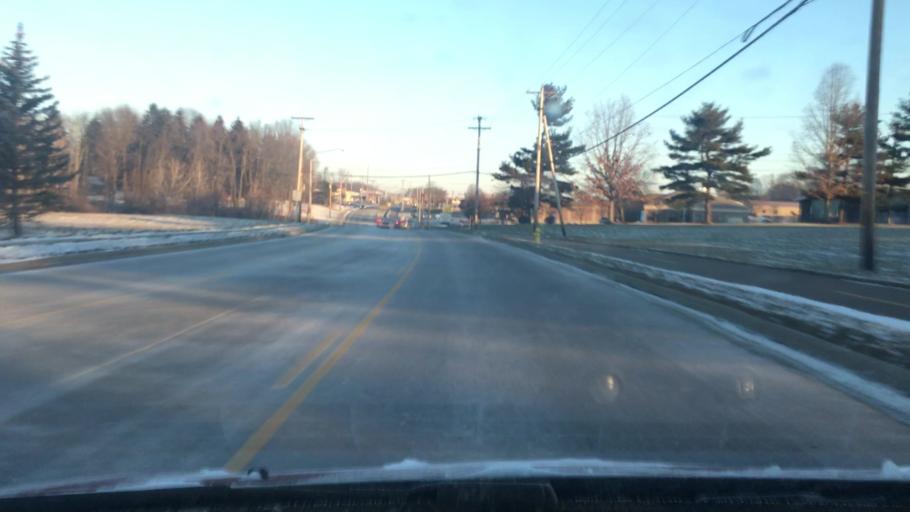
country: US
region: Ohio
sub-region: Wayne County
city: Wooster
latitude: 40.8242
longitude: -81.9078
